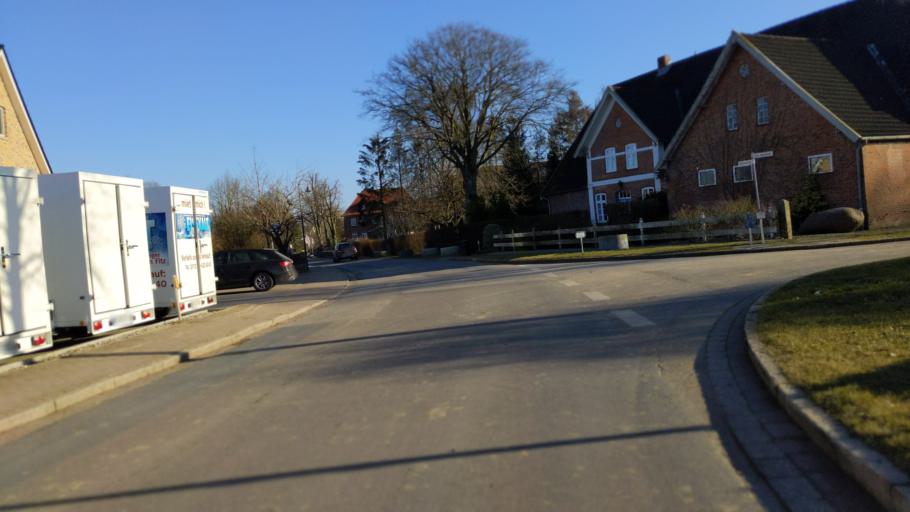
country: DE
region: Schleswig-Holstein
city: Ahrensbok
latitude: 54.0161
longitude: 10.6447
